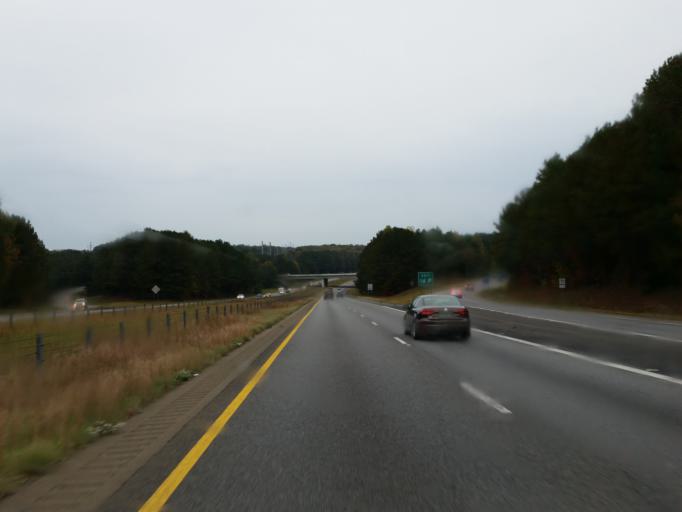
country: US
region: Georgia
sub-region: Cherokee County
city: Holly Springs
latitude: 34.1847
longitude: -84.5065
